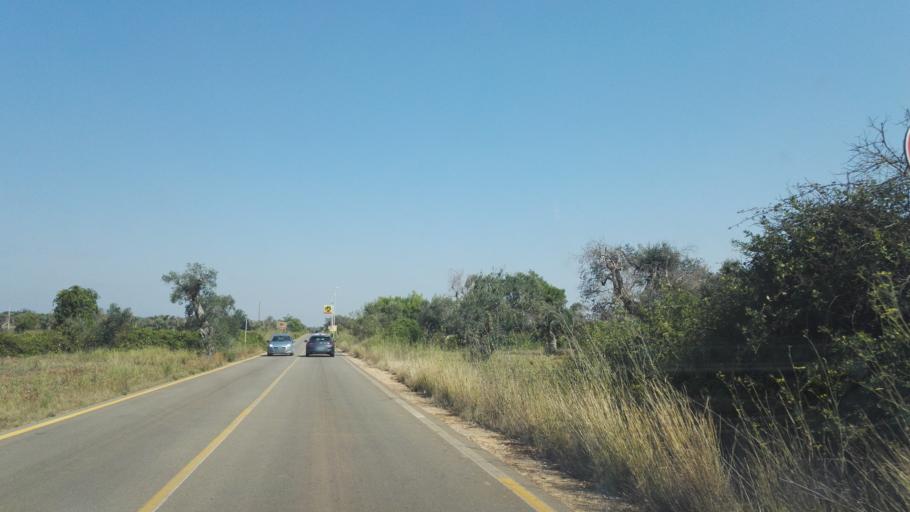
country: IT
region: Apulia
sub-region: Provincia di Lecce
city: Nardo
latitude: 40.1837
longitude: 17.9726
